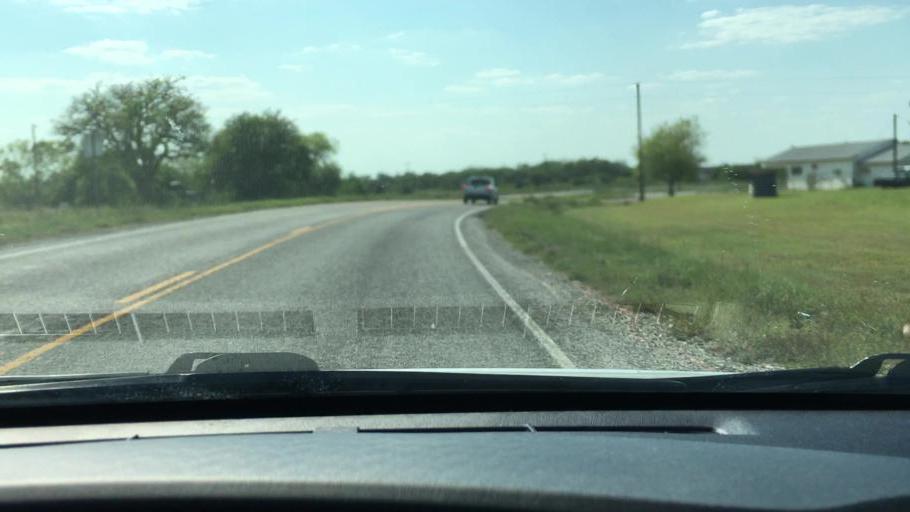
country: US
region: Texas
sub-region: DeWitt County
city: Yorktown
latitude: 28.9188
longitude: -97.3446
